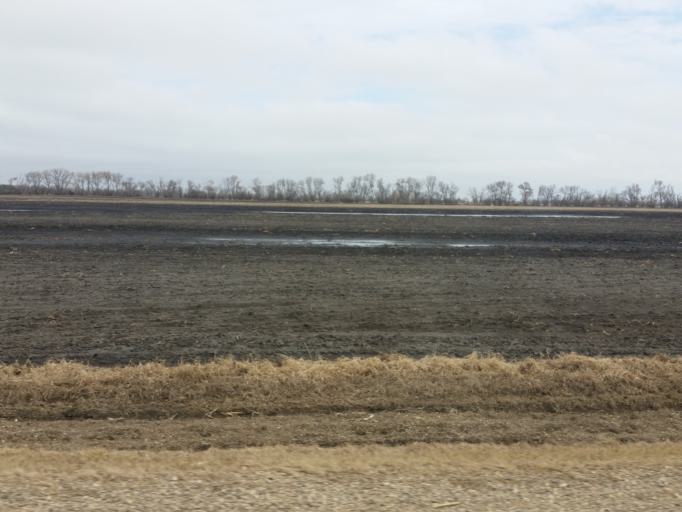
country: US
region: North Dakota
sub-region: Walsh County
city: Grafton
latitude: 48.4243
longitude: -97.3212
